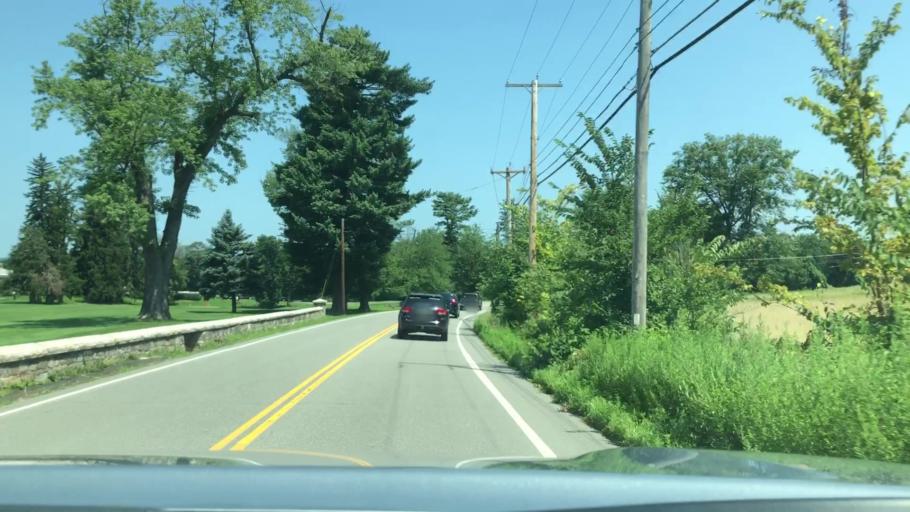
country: US
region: New York
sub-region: Orange County
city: Highland Falls
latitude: 41.3712
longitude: -73.9469
